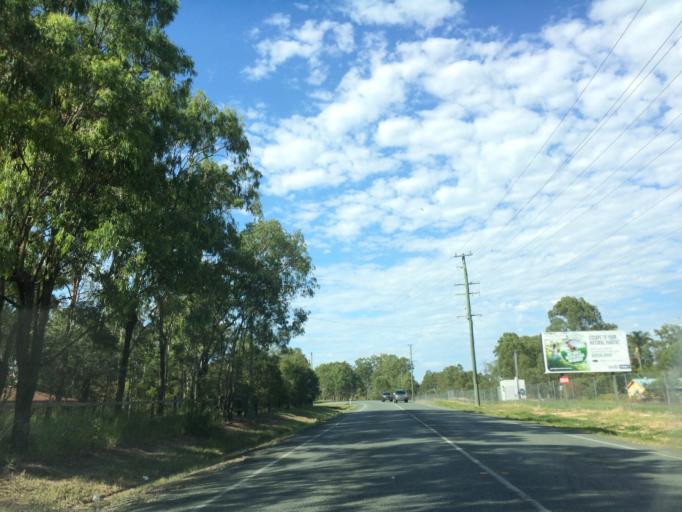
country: AU
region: Queensland
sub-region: Logan
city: Park Ridge South
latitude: -27.7235
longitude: 152.9855
